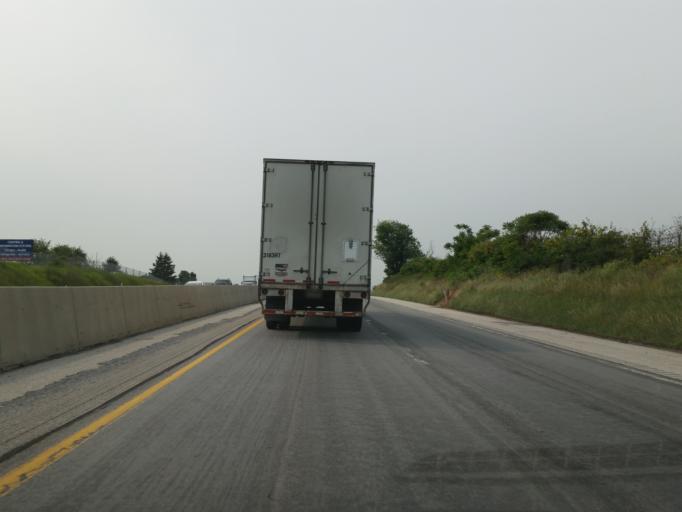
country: US
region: Pennsylvania
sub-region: York County
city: Emigsville
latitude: 40.0486
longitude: -76.7521
